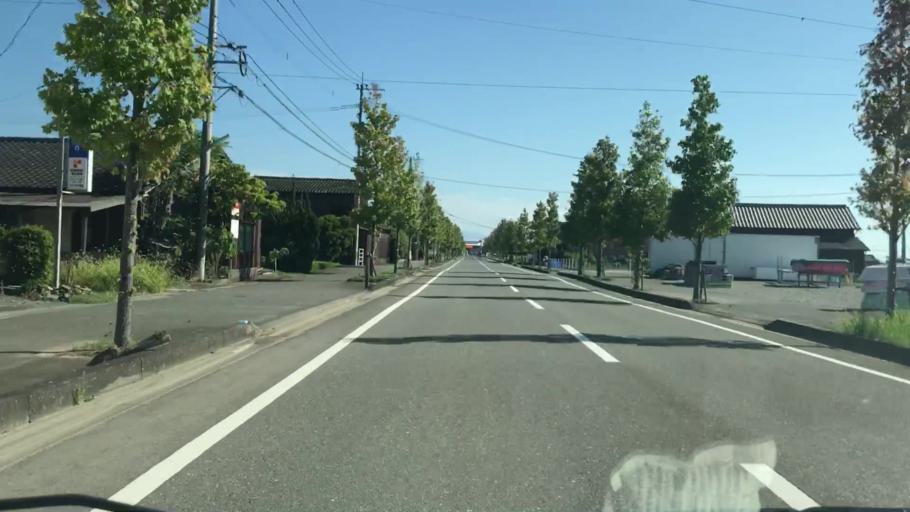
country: JP
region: Saga Prefecture
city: Okawa
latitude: 33.1857
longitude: 130.3138
